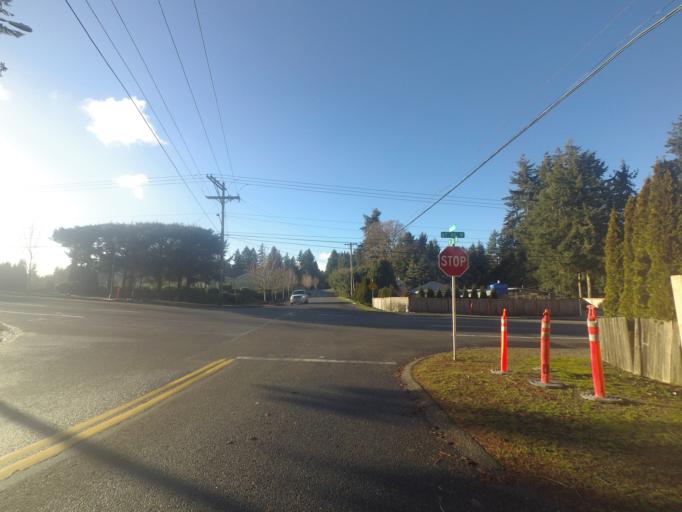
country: US
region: Washington
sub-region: Pierce County
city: Fircrest
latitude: 47.2246
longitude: -122.5260
